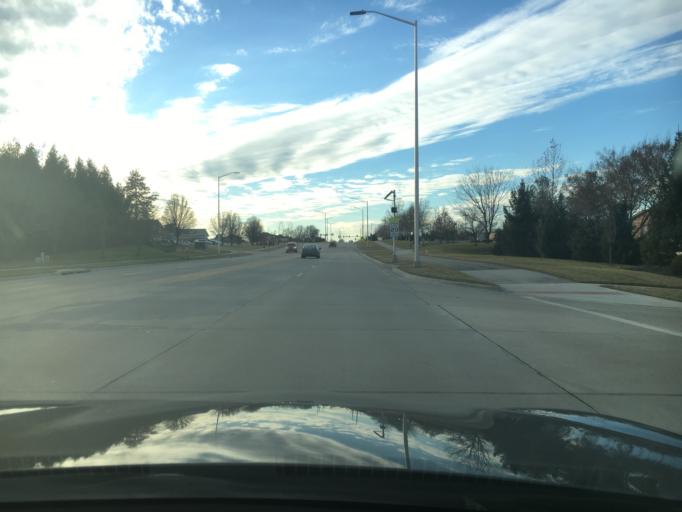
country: US
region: Kansas
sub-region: Johnson County
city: Leawood
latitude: 38.8693
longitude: -94.6448
